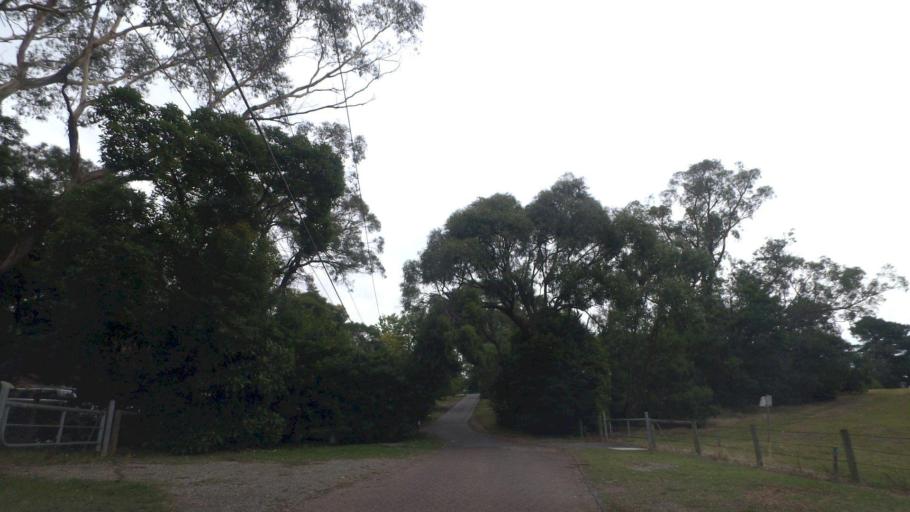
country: AU
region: Victoria
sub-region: Yarra Ranges
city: Kilsyth
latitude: -37.7929
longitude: 145.3369
